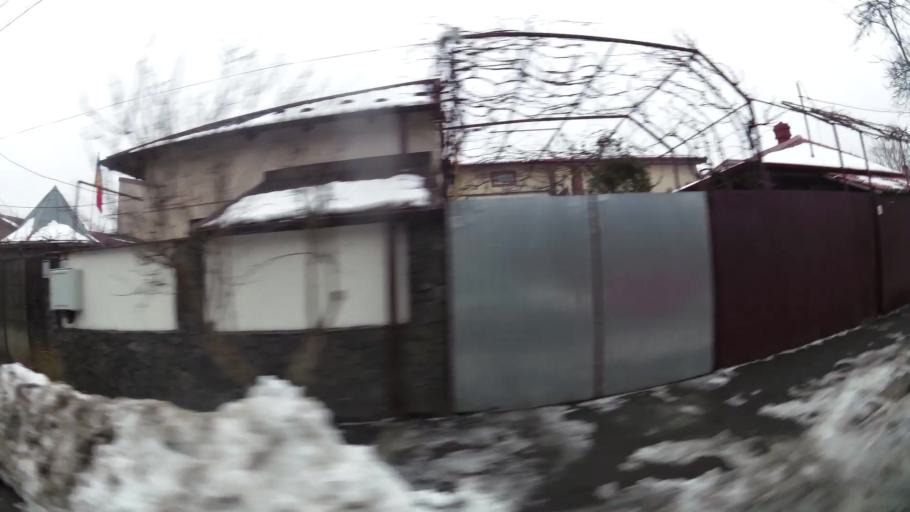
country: RO
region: Ilfov
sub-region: Comuna Chiajna
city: Rosu
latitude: 44.4794
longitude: 26.0297
